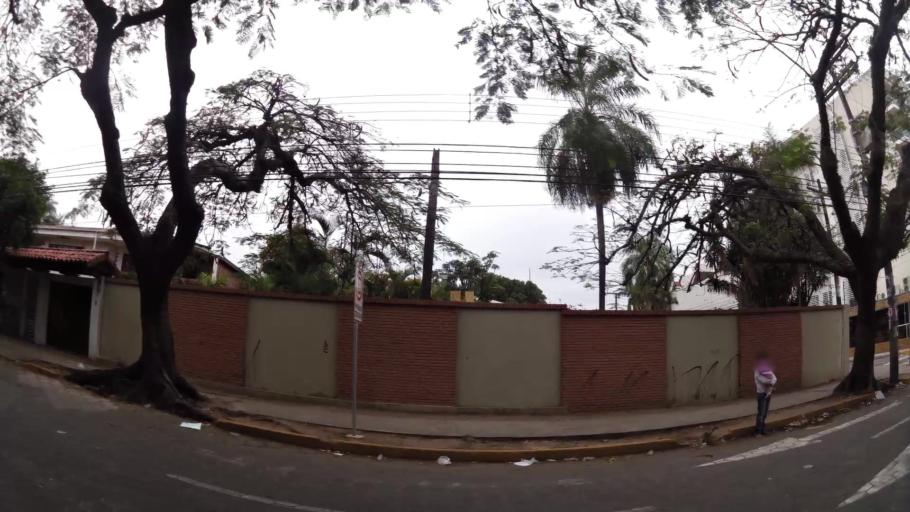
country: BO
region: Santa Cruz
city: Santa Cruz de la Sierra
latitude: -17.7974
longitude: -63.1806
